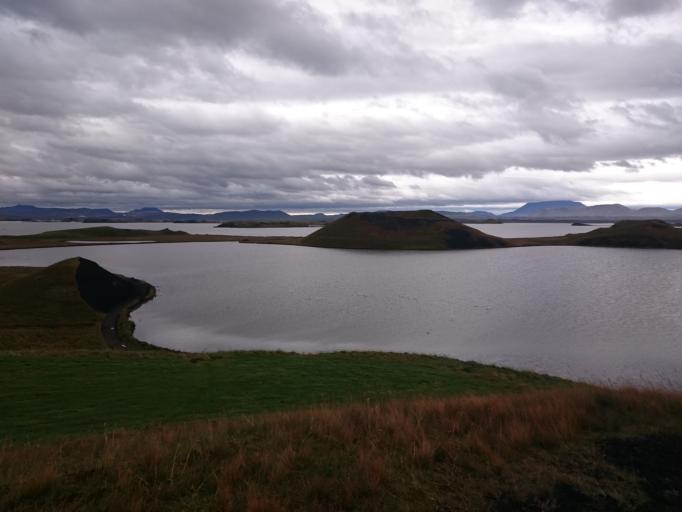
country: IS
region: Northeast
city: Laugar
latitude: 65.5708
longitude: -17.0314
